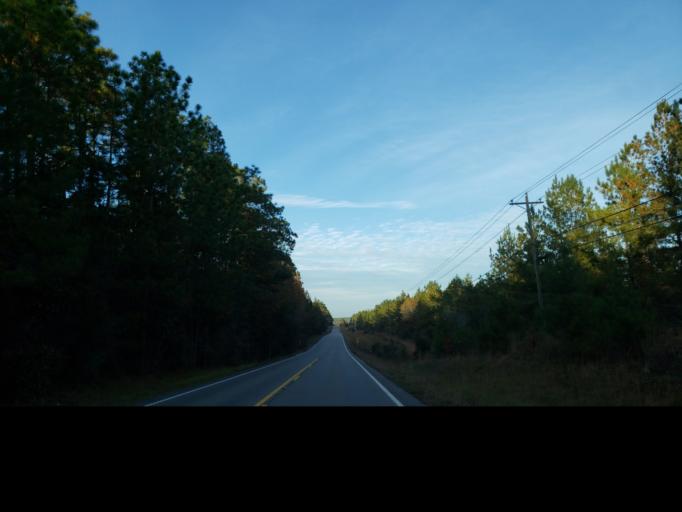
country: US
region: Mississippi
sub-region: Lamar County
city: Purvis
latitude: 31.1757
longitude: -89.3868
